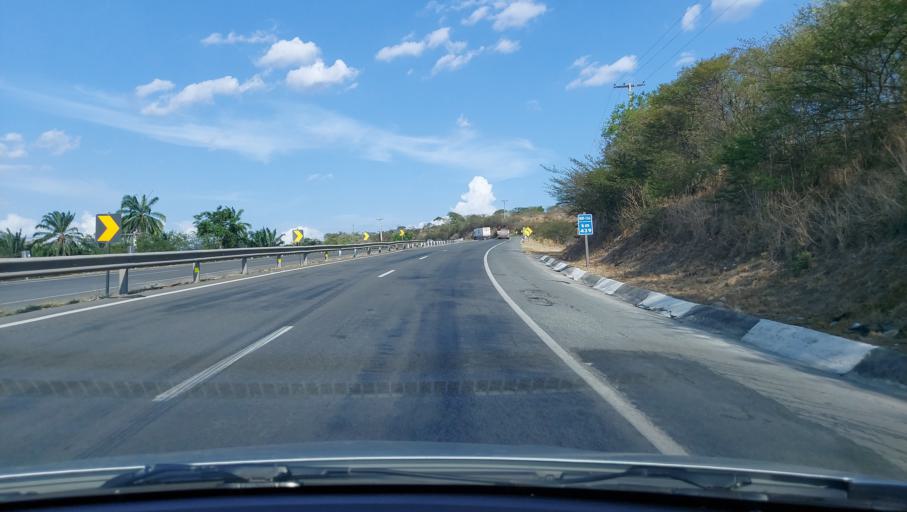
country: BR
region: Bahia
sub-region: Feira De Santana
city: Feira de Santana
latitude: -12.3372
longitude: -39.0757
